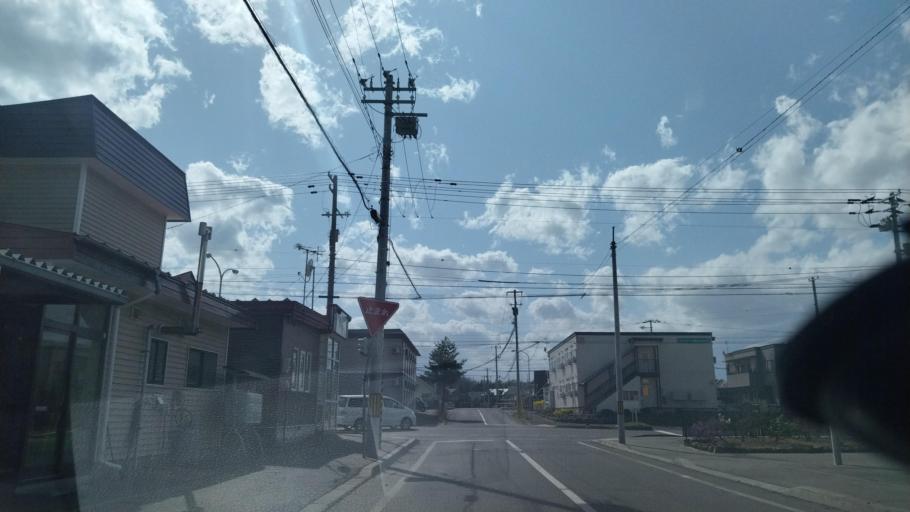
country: JP
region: Hokkaido
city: Obihiro
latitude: 42.9053
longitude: 143.1467
